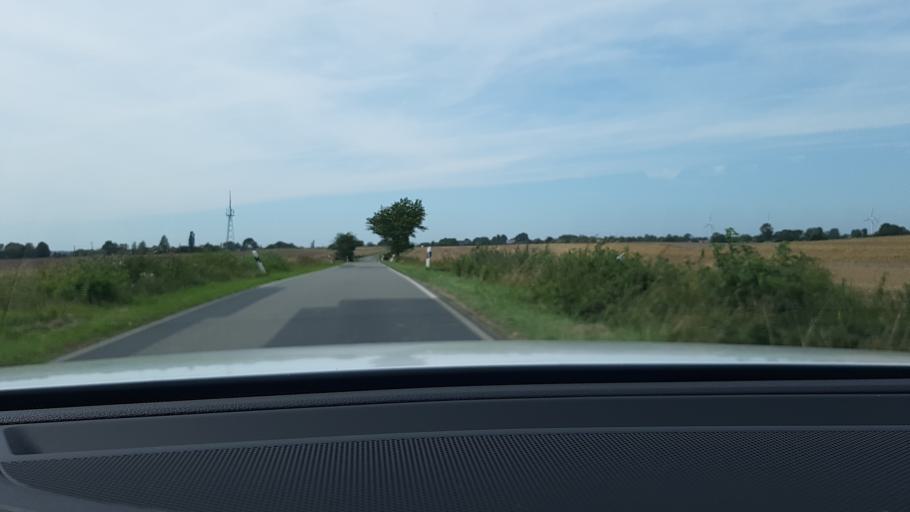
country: DE
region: Schleswig-Holstein
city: Rehhorst
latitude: 53.8712
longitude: 10.4839
